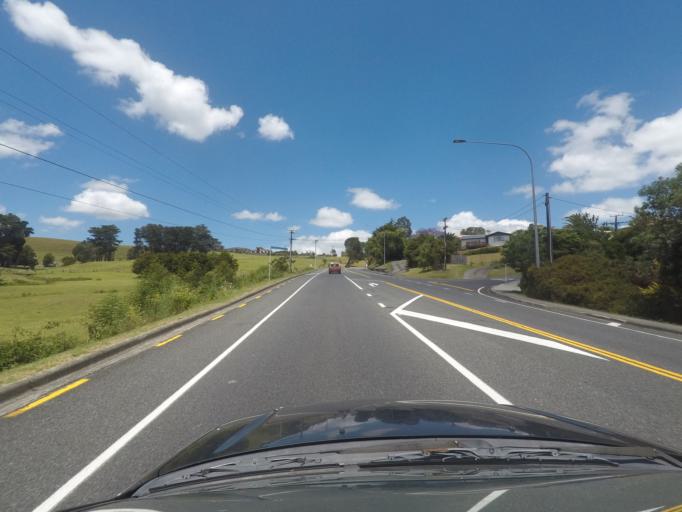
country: NZ
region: Northland
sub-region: Whangarei
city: Whangarei
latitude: -35.7416
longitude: 174.3643
